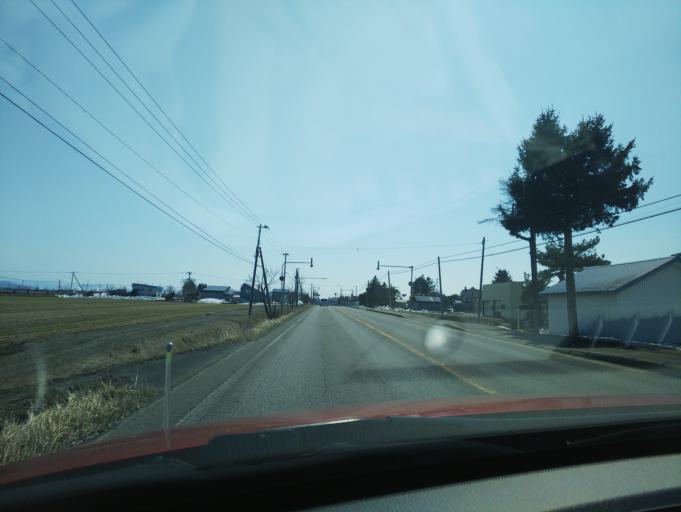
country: JP
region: Hokkaido
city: Nayoro
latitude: 44.2477
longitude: 142.3947
